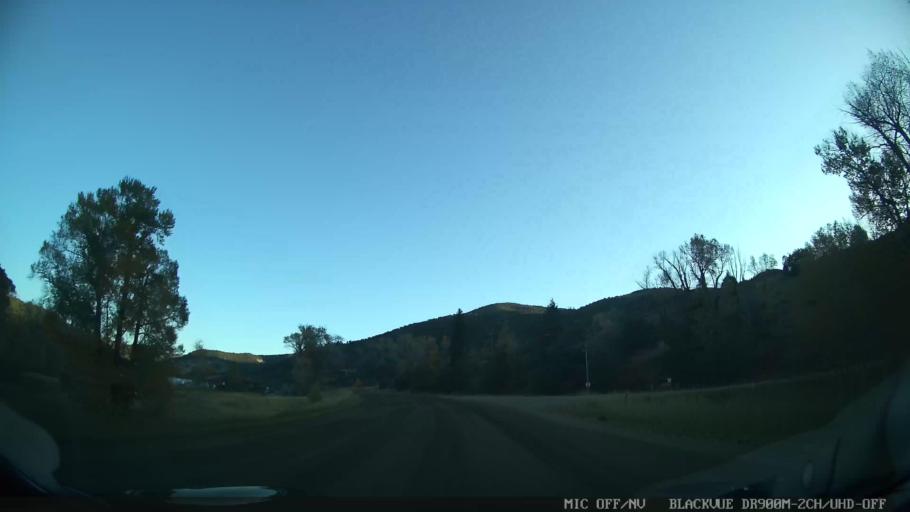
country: US
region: Colorado
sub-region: Grand County
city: Kremmling
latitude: 39.9295
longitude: -106.5268
